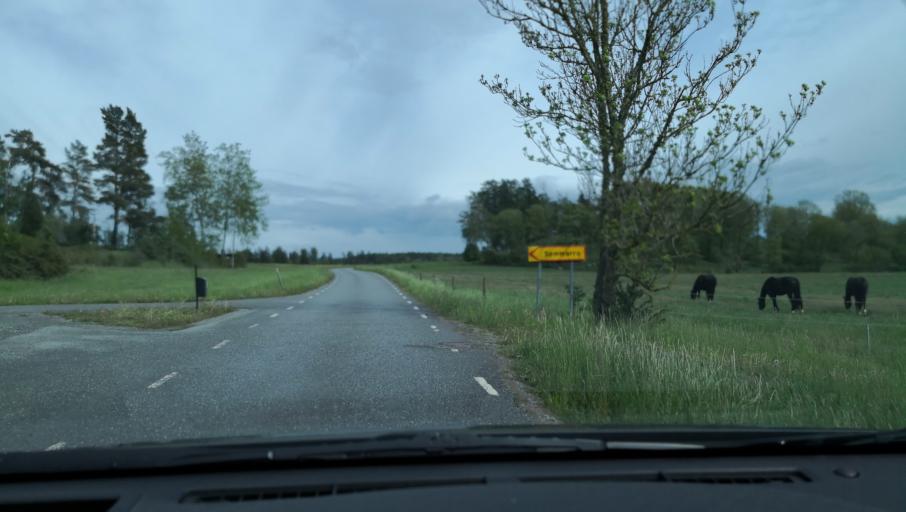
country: SE
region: Uppsala
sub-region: Enkopings Kommun
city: Orsundsbro
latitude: 59.7052
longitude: 17.4075
